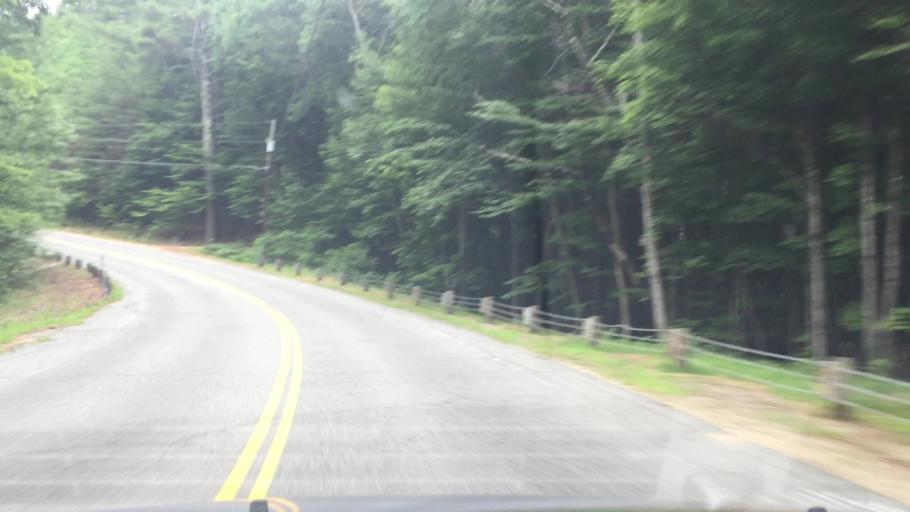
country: US
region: New Hampshire
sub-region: Carroll County
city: North Conway
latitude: 44.0852
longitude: -71.1656
